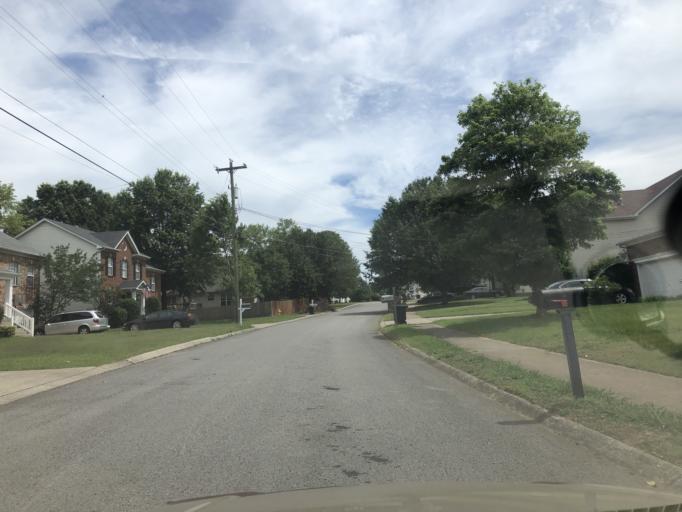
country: US
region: Tennessee
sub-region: Davidson County
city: Lakewood
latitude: 36.2537
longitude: -86.6081
